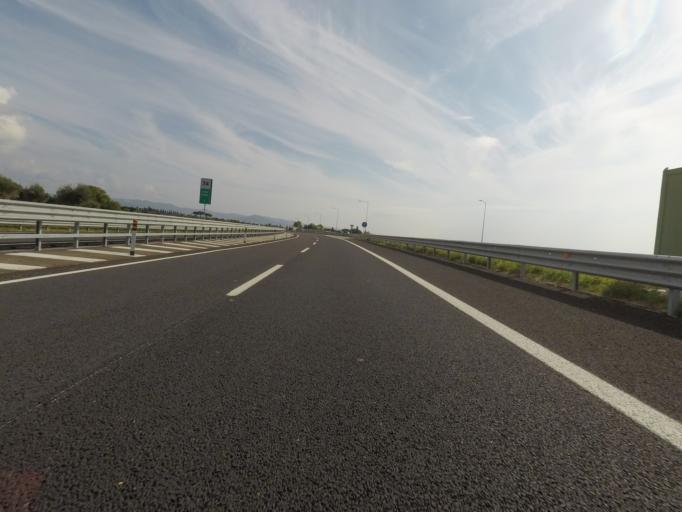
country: IT
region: Latium
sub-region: Provincia di Viterbo
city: Tarquinia
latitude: 42.2361
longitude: 11.7615
